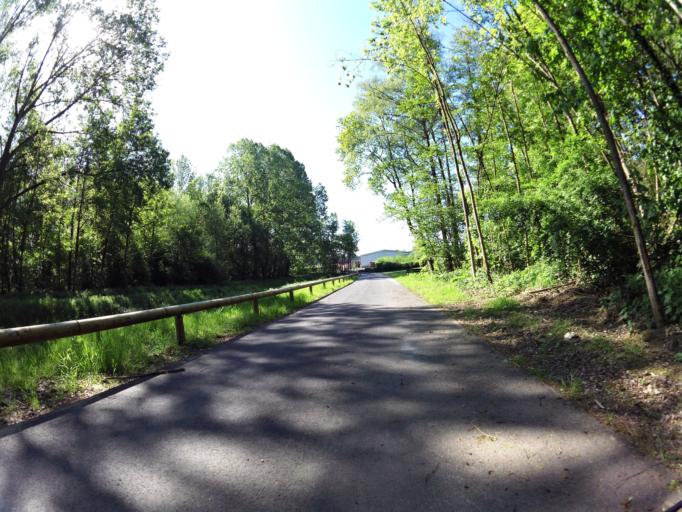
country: NL
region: Limburg
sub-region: Gemeente Nuth
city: Nuth
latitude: 50.9288
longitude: 5.8920
